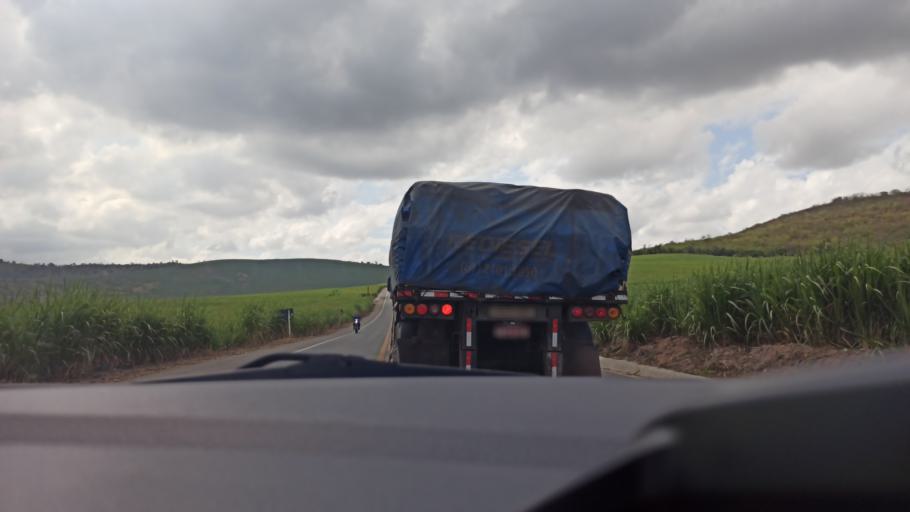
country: BR
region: Pernambuco
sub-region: Timbauba
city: Timbauba
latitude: -7.5243
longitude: -35.2919
